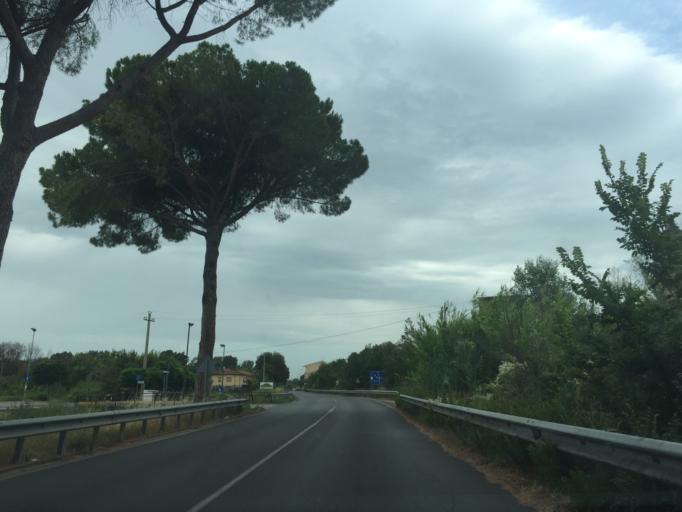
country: IT
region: Tuscany
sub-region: Province of Pisa
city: Uliveto Terme
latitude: 43.7042
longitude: 10.5077
